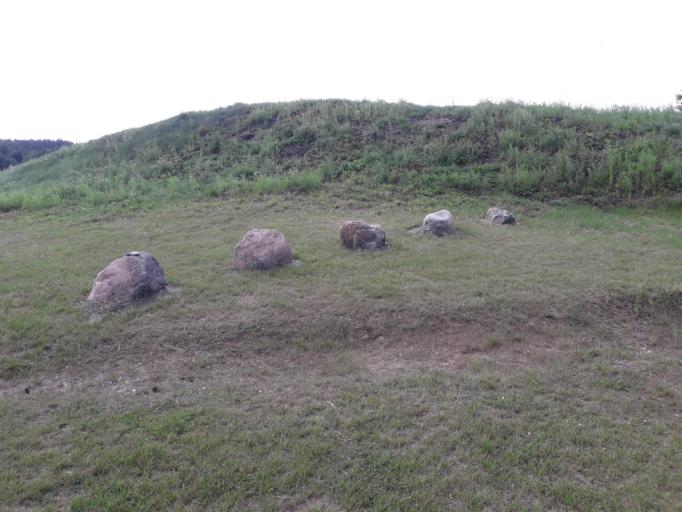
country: LT
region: Alytaus apskritis
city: Druskininkai
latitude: 54.0686
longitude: 24.0497
